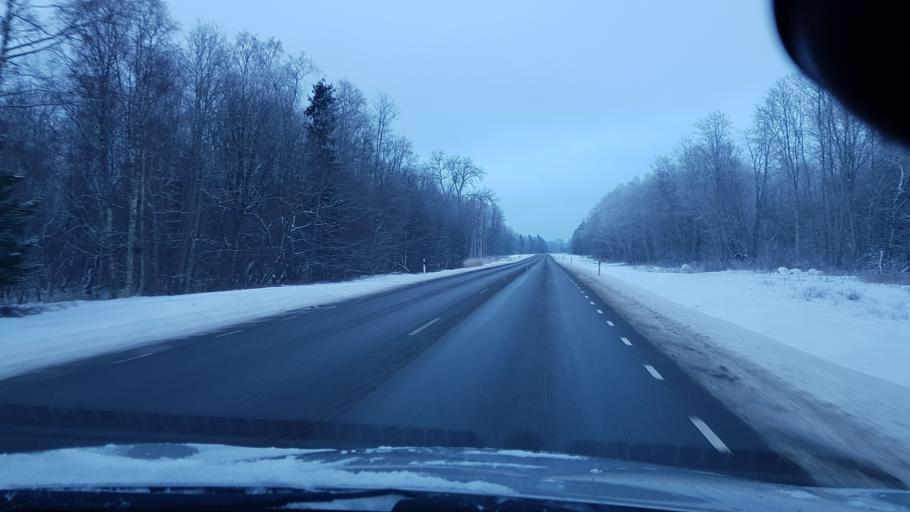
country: EE
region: Harju
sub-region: Paldiski linn
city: Paldiski
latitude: 59.3428
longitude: 24.1708
